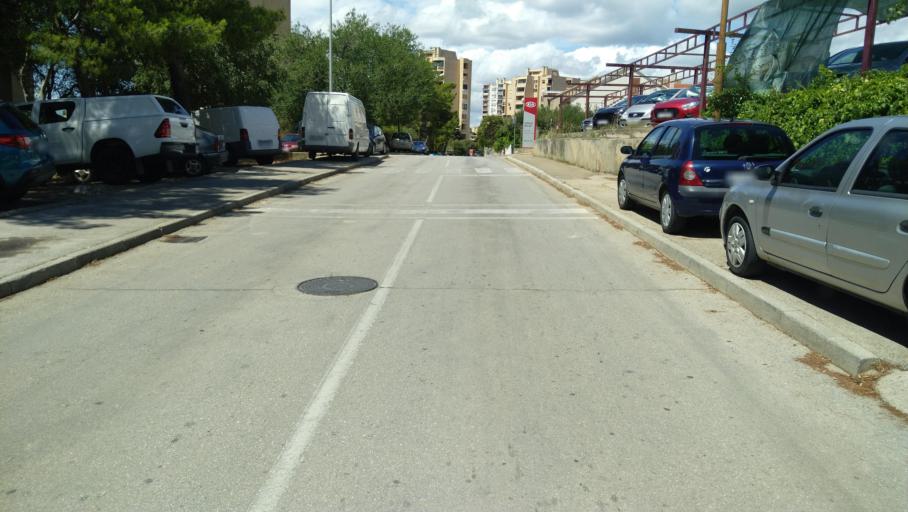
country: HR
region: Sibensko-Kniniska
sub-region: Grad Sibenik
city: Sibenik
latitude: 43.7214
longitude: 15.9117
